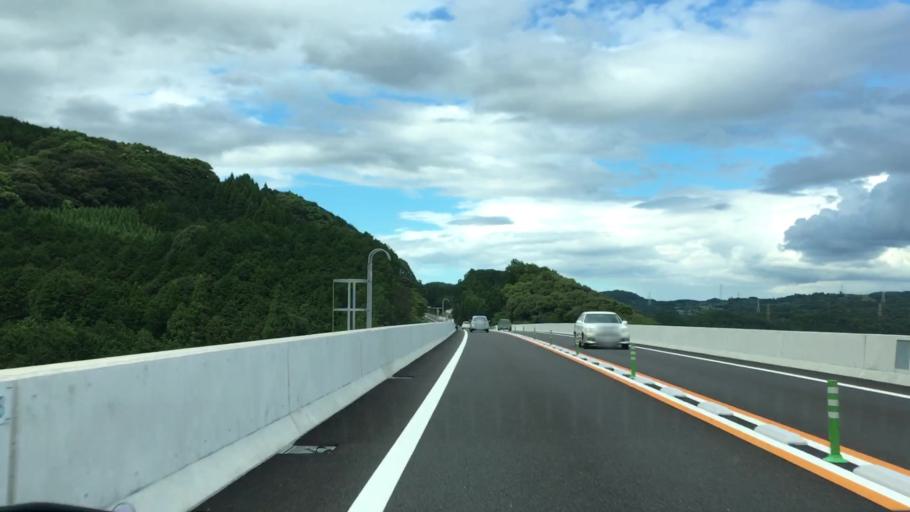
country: JP
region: Saga Prefecture
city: Imaricho-ko
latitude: 33.3243
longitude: 129.9270
